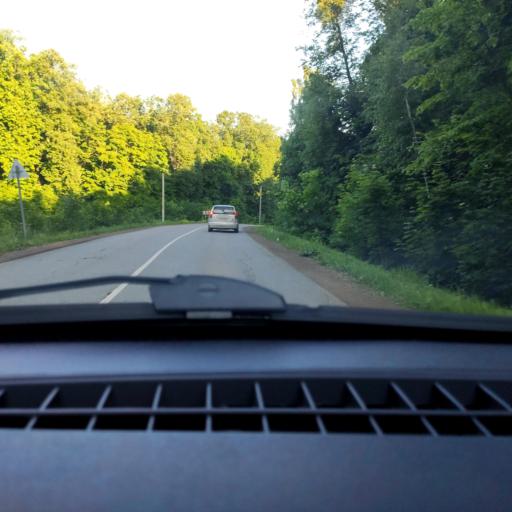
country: RU
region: Bashkortostan
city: Avdon
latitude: 54.6534
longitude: 55.7013
